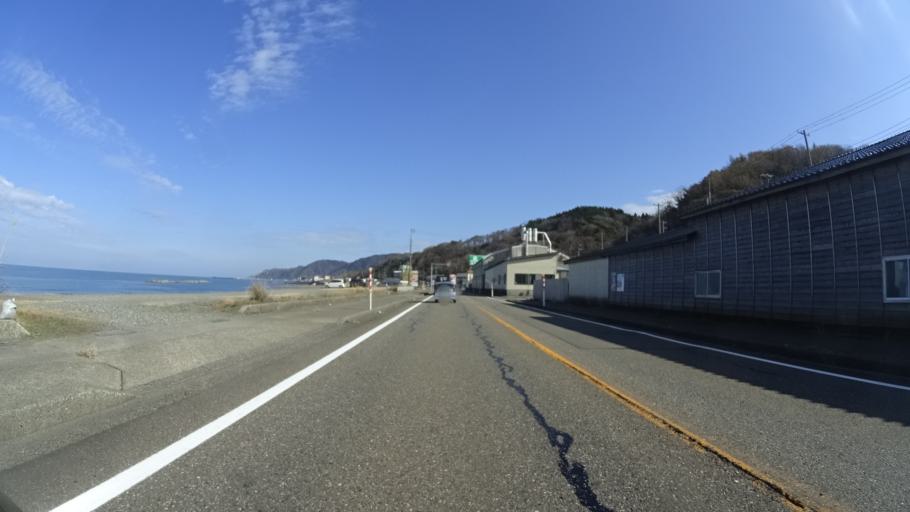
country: JP
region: Niigata
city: Itoigawa
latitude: 37.1148
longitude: 138.0240
